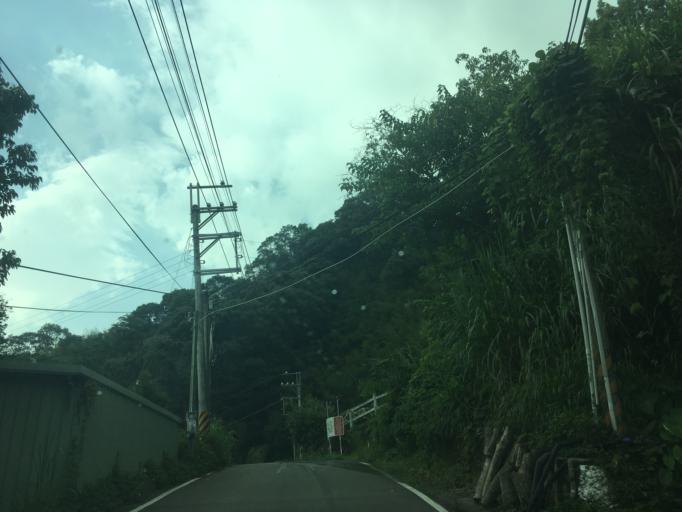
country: TW
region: Taiwan
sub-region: Miaoli
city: Miaoli
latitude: 24.3931
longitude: 120.9791
